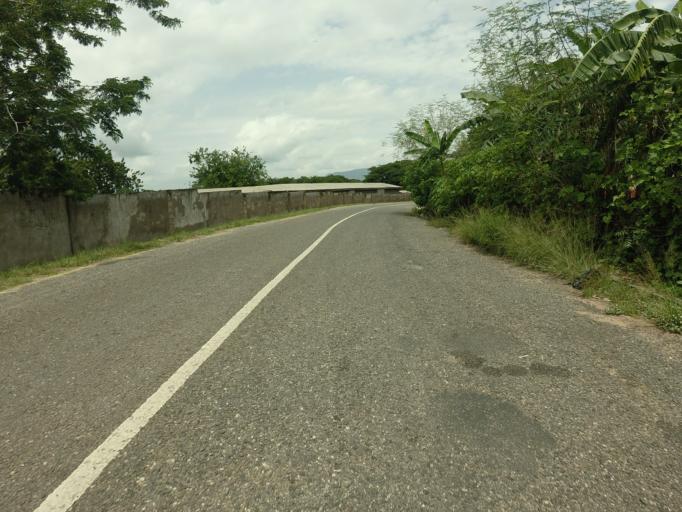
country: GH
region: Volta
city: Ho
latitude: 6.5941
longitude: 0.4776
